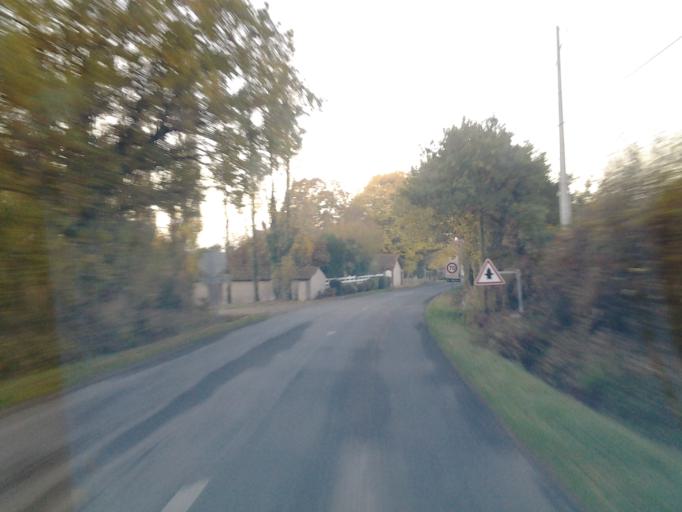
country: FR
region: Pays de la Loire
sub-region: Departement de la Vendee
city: Chateau-Guibert
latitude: 46.6235
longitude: -1.2328
